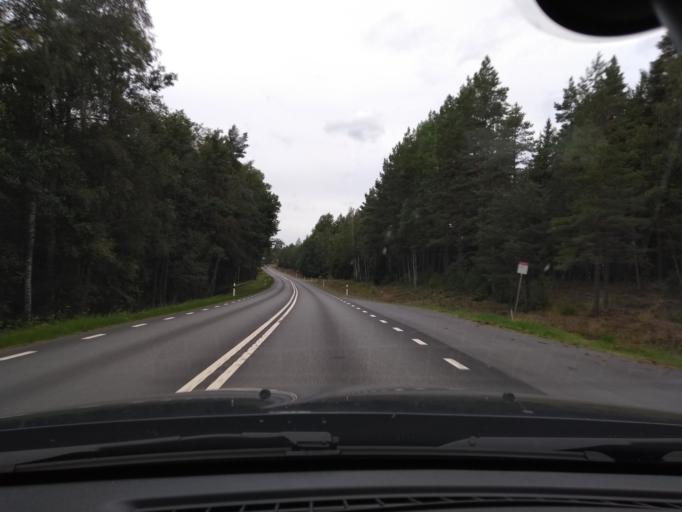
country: SE
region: Joenkoeping
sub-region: Eksjo Kommun
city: Haljarp
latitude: 57.6350
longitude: 15.3310
